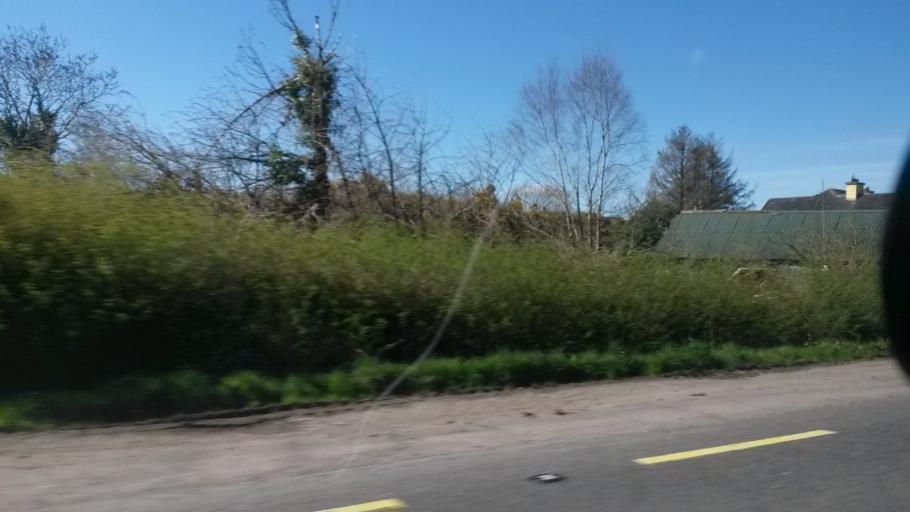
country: IE
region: Munster
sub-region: County Cork
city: Macroom
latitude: 51.9164
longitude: -9.0579
